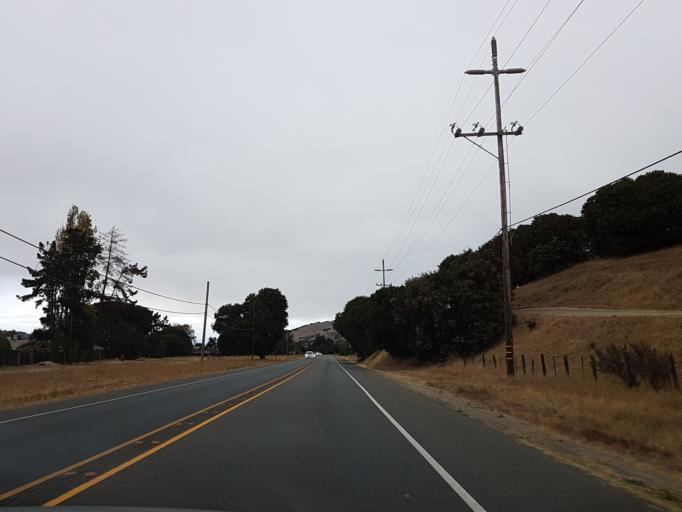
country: US
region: California
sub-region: Monterey County
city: Carmel Valley Village
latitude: 36.5901
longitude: -121.7090
